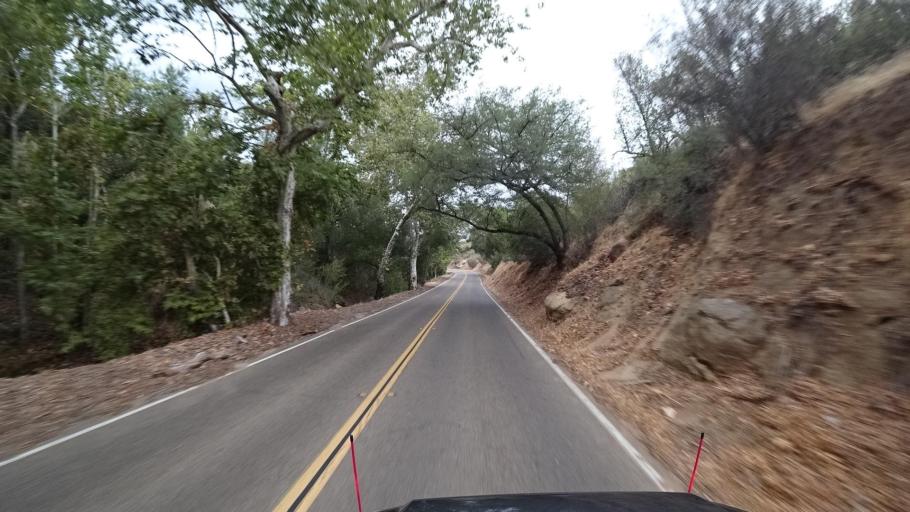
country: US
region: California
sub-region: San Diego County
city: Ramona
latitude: 32.9935
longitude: -116.9280
